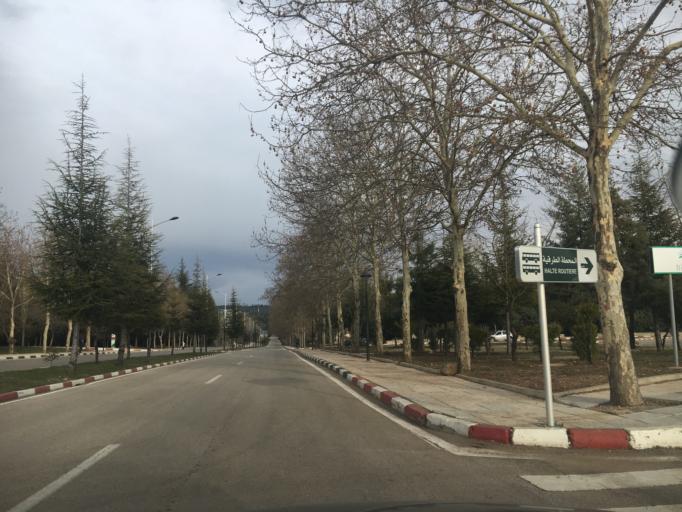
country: MA
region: Meknes-Tafilalet
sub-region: Ifrane
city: Ifrane
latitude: 33.5279
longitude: -5.1248
